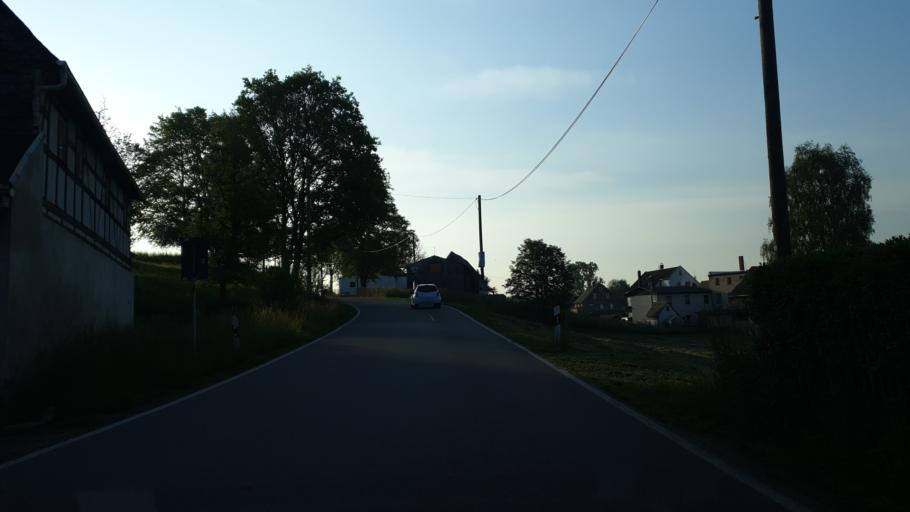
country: DE
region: Saxony
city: Bernsdorf
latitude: 50.7850
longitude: 12.6644
